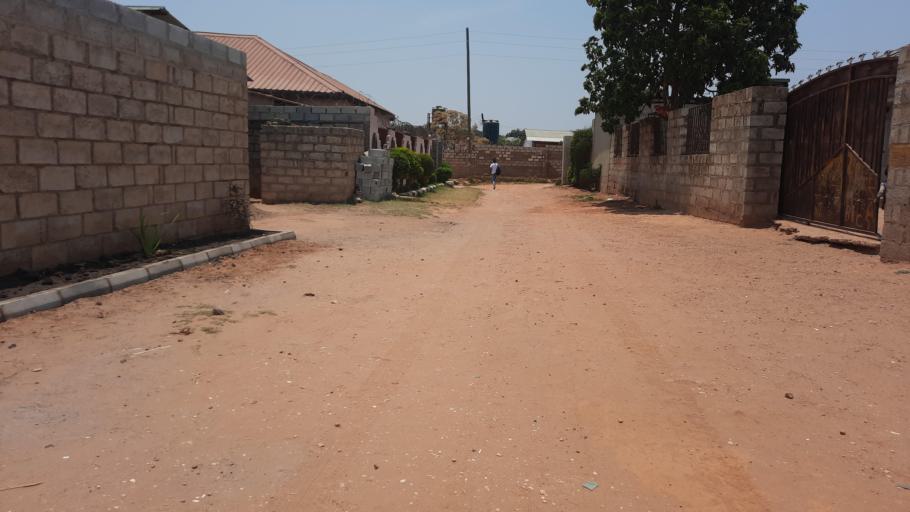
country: ZM
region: Lusaka
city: Lusaka
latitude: -15.4059
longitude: 28.3826
